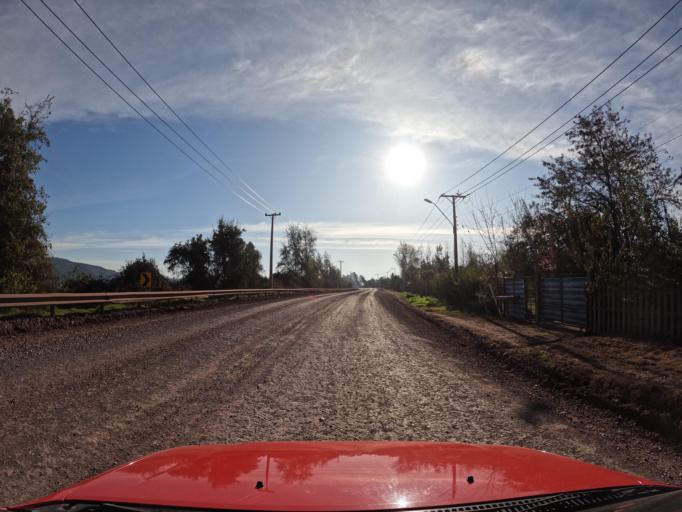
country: CL
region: Maule
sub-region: Provincia de Curico
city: Teno
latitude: -34.9624
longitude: -70.9595
